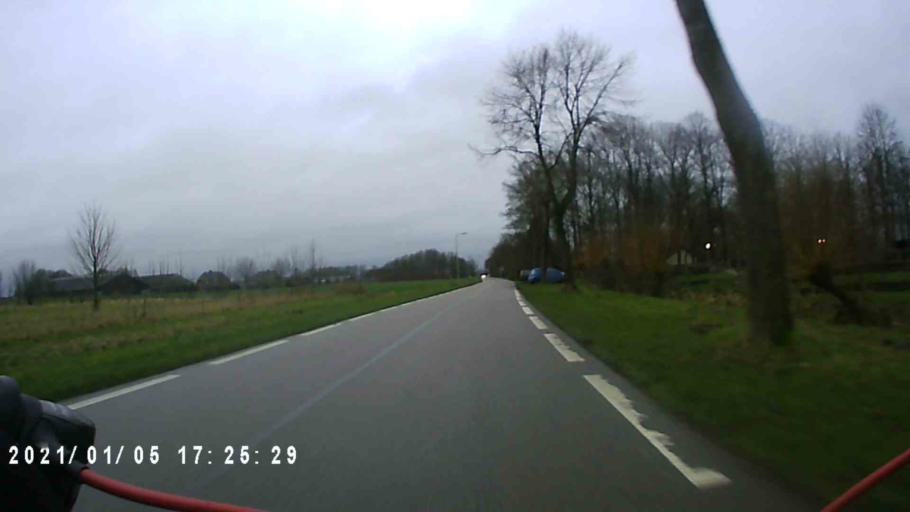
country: NL
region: Groningen
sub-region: Gemeente Delfzijl
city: Delfzijl
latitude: 53.2289
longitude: 6.9610
